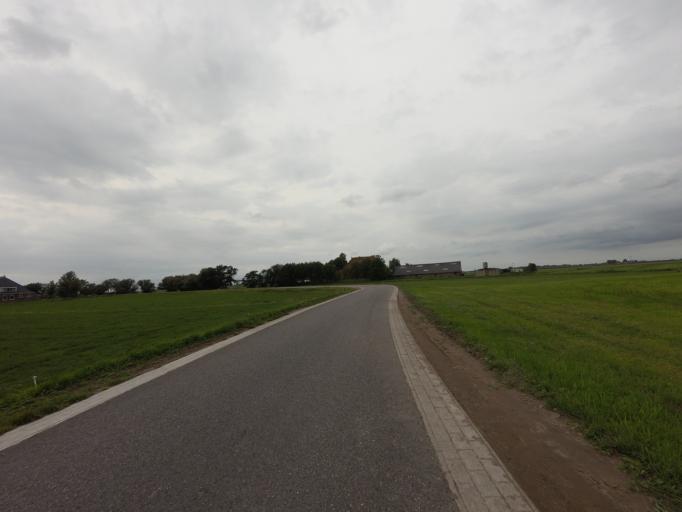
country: NL
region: Friesland
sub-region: Sudwest Fryslan
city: Bolsward
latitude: 53.0255
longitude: 5.5245
